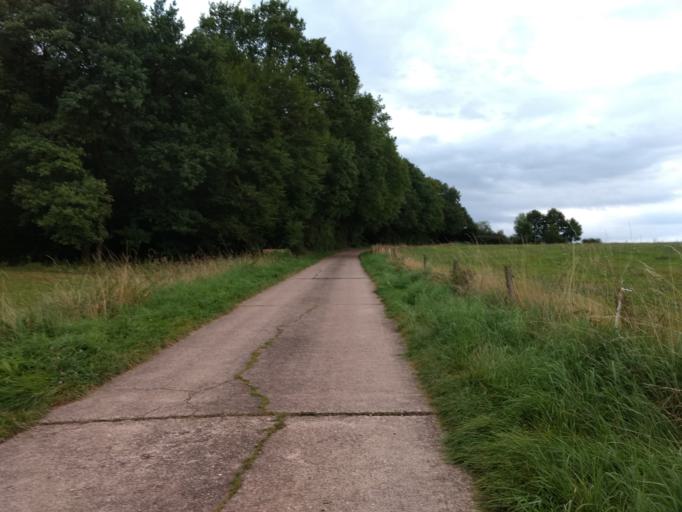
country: DE
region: Saarland
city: Schmelz
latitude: 49.3855
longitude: 6.8430
